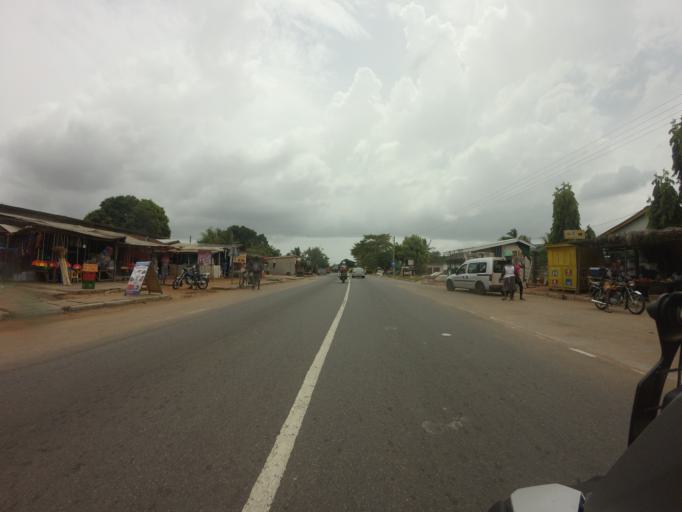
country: GH
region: Volta
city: Keta
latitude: 6.0650
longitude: 0.8617
